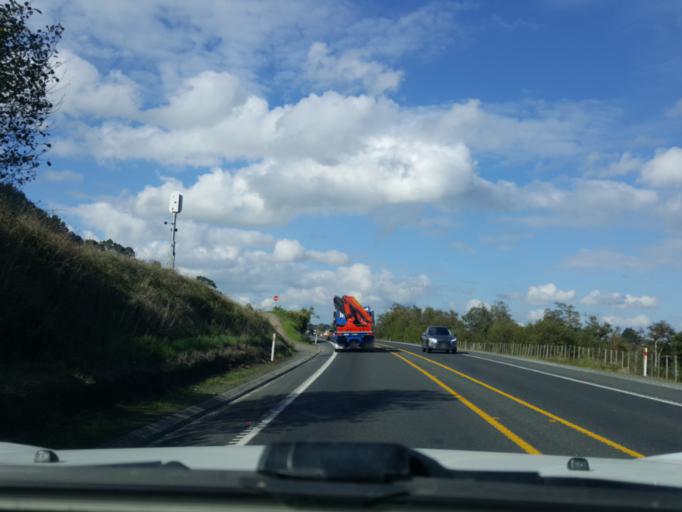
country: NZ
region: Waikato
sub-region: Waikato District
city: Ngaruawahia
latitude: -37.6029
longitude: 175.1730
